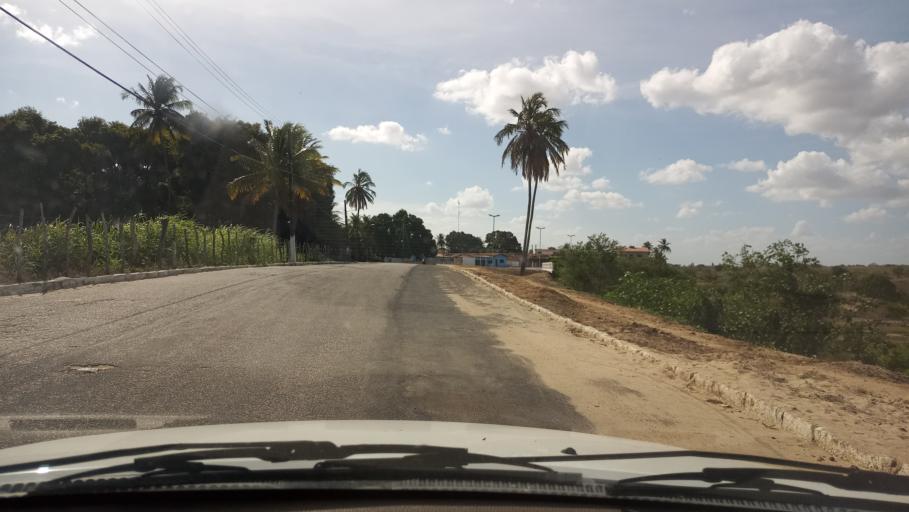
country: BR
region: Rio Grande do Norte
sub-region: Goianinha
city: Goianinha
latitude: -6.3323
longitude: -35.3042
